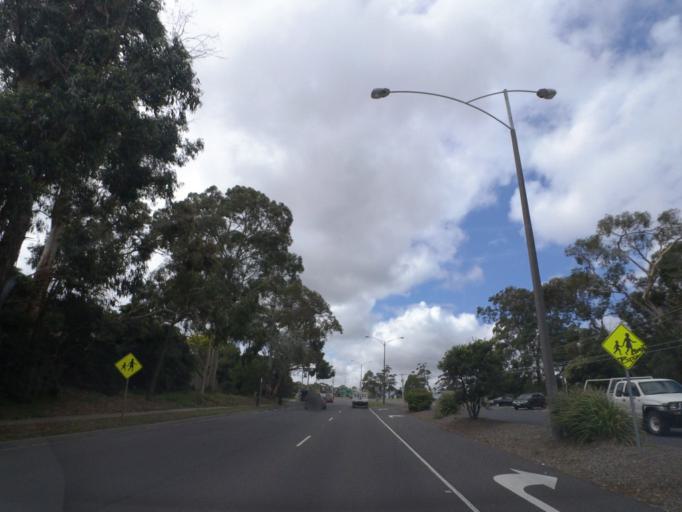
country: AU
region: Victoria
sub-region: Banyule
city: Greensborough
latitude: -37.6912
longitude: 145.1137
